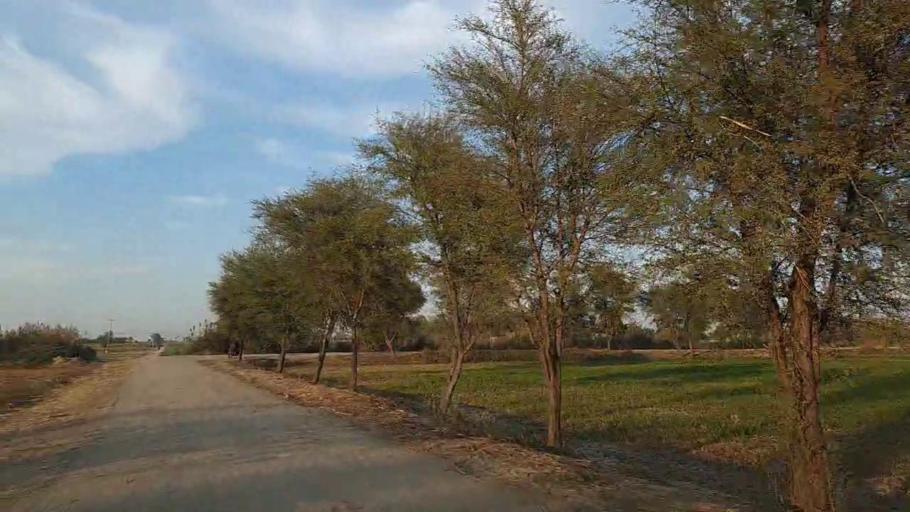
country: PK
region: Sindh
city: Bandhi
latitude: 26.5975
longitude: 68.3478
